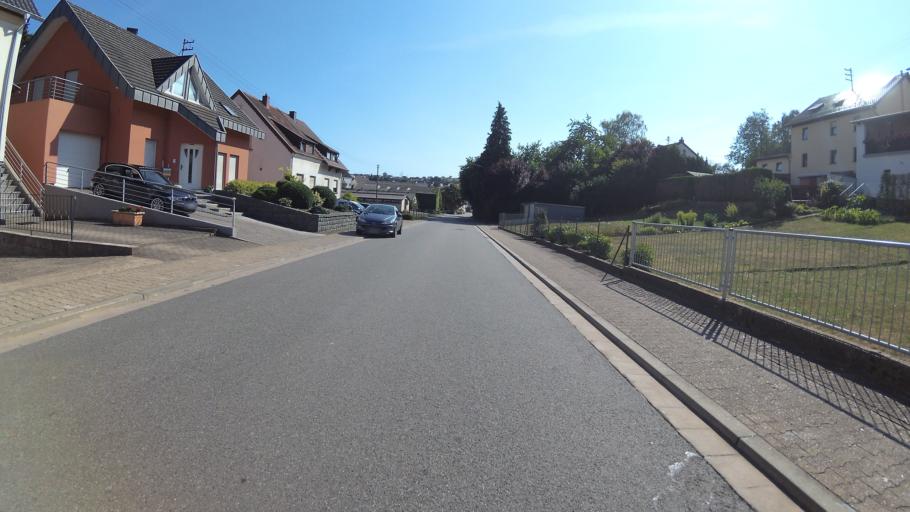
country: DE
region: Saarland
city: Eppelborn
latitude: 49.4153
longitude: 6.9521
